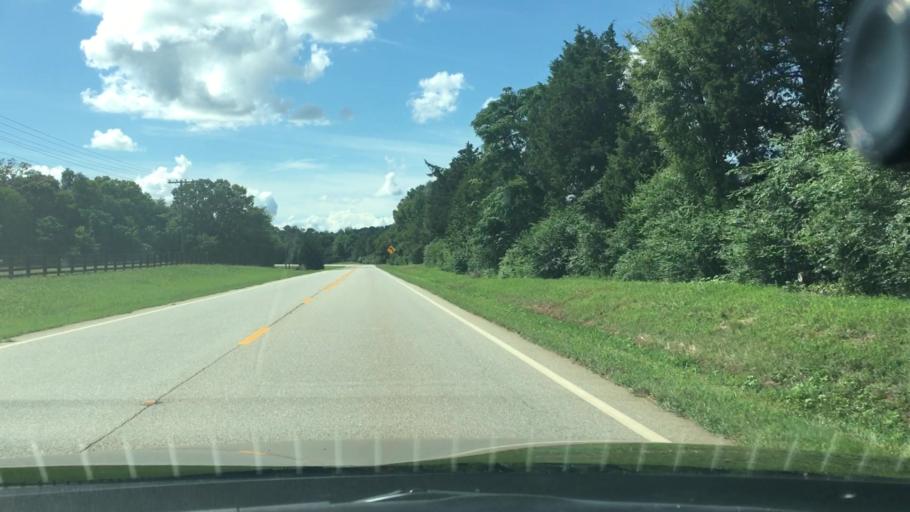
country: US
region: Georgia
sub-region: Jasper County
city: Monticello
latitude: 33.3142
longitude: -83.7497
